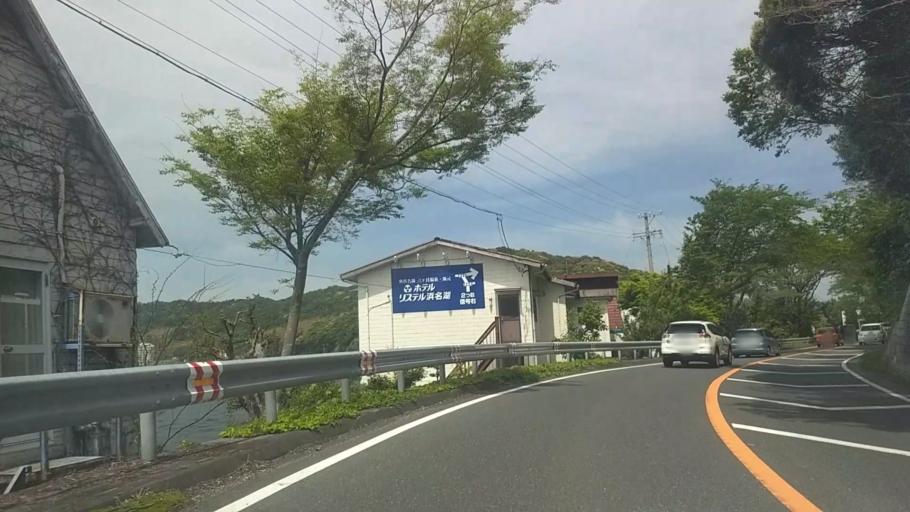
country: JP
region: Shizuoka
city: Kosai-shi
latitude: 34.7674
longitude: 137.5498
